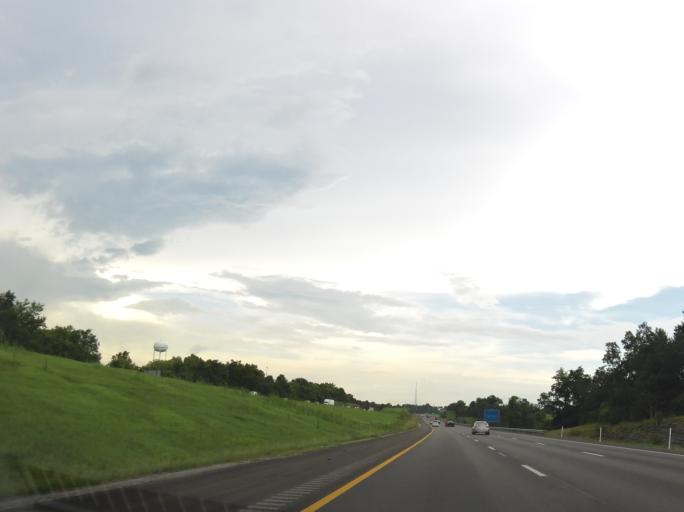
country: US
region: Kentucky
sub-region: Madison County
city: Richmond
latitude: 37.8615
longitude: -84.3319
